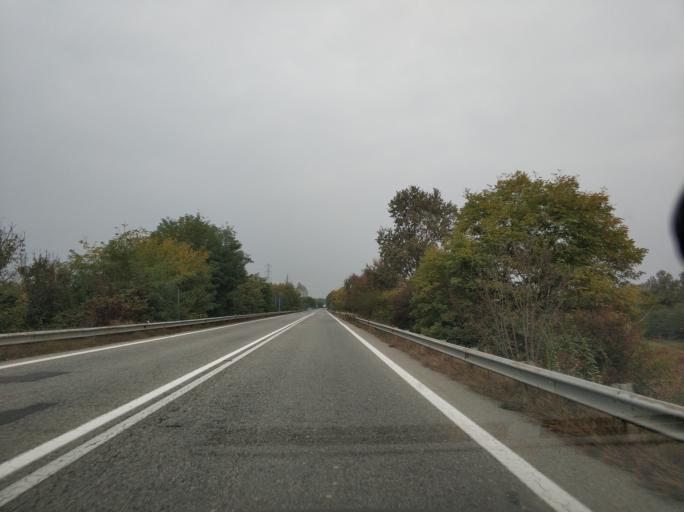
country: IT
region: Piedmont
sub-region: Provincia di Torino
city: Lombardore
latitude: 45.2348
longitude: 7.7473
